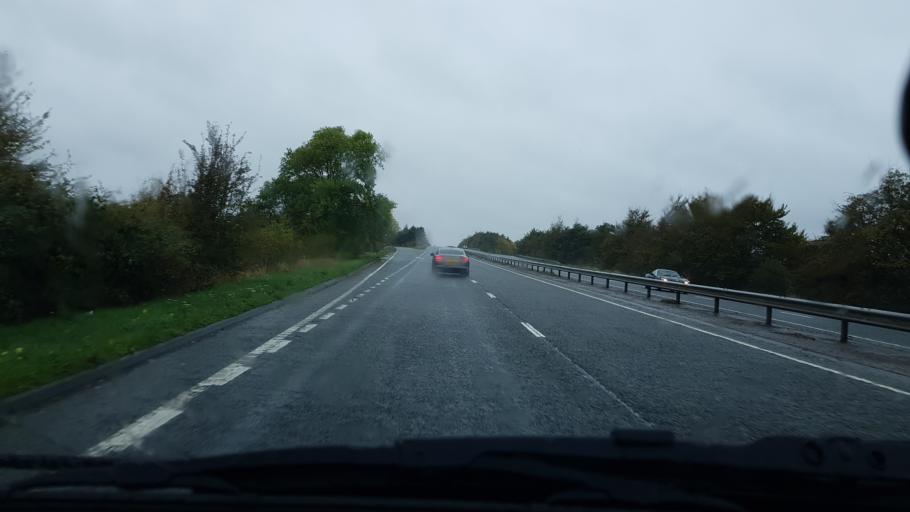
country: GB
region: England
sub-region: Oxfordshire
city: Carterton
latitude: 51.7819
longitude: -1.5474
